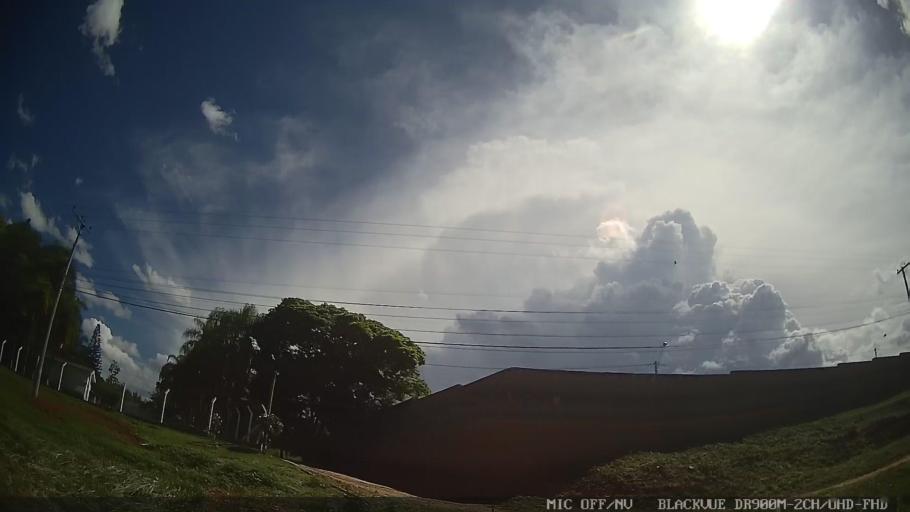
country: BR
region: Sao Paulo
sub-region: Pedreira
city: Pedreira
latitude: -22.7346
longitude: -46.8763
